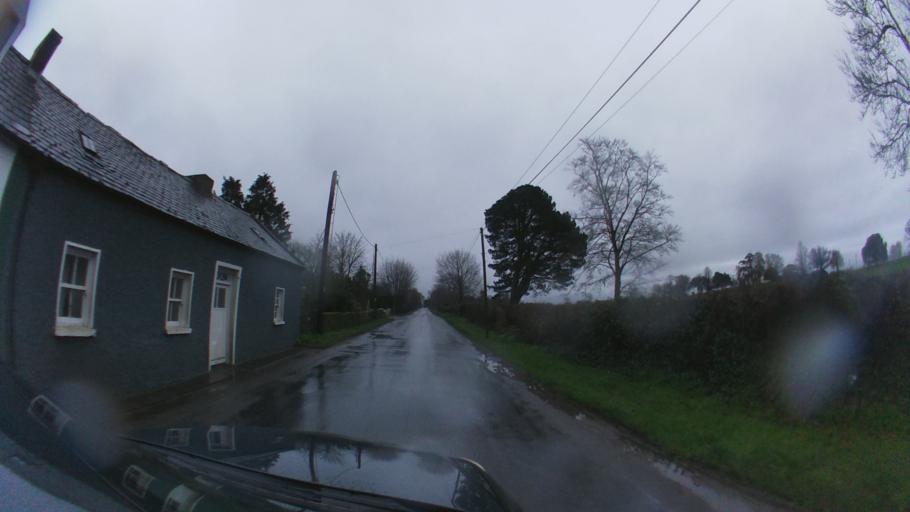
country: IE
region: Leinster
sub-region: County Carlow
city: Bagenalstown
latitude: 52.6529
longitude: -6.9895
